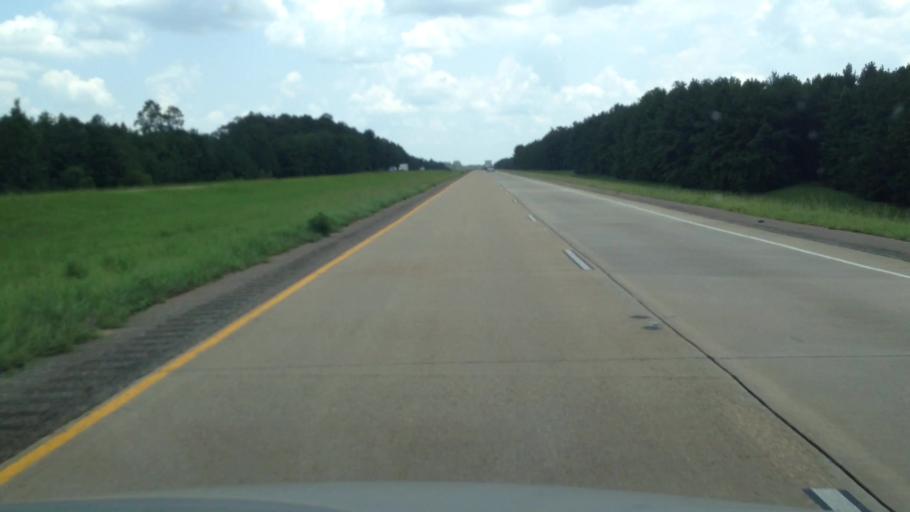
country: US
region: Louisiana
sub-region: Rapides Parish
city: Lecompte
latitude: 31.0544
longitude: -92.4240
